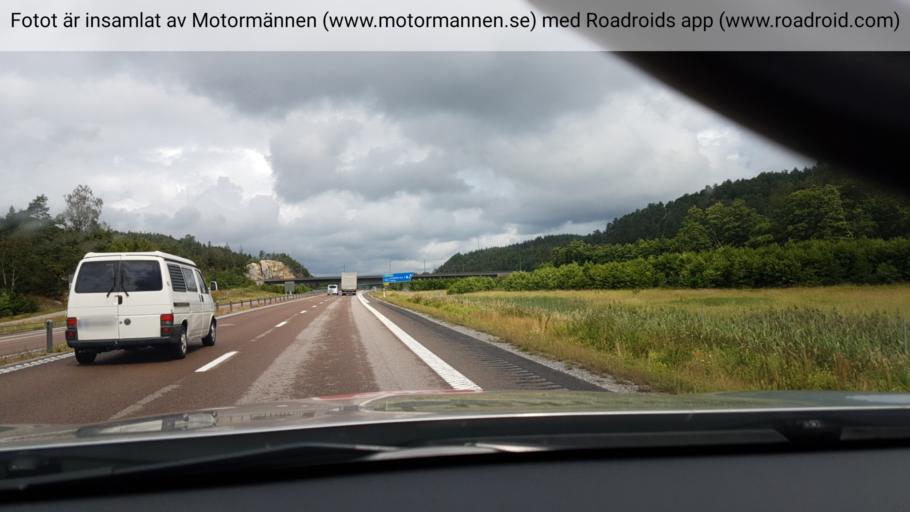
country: SE
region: Vaestra Goetaland
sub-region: Stromstads Kommun
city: Stroemstad
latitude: 58.9263
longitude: 11.2560
